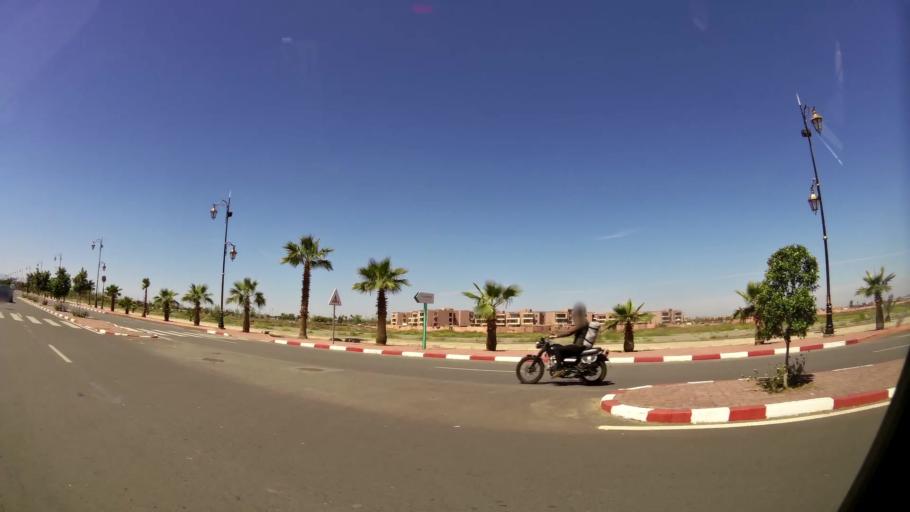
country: MA
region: Marrakech-Tensift-Al Haouz
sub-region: Marrakech
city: Marrakesh
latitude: 31.5989
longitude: -7.9912
